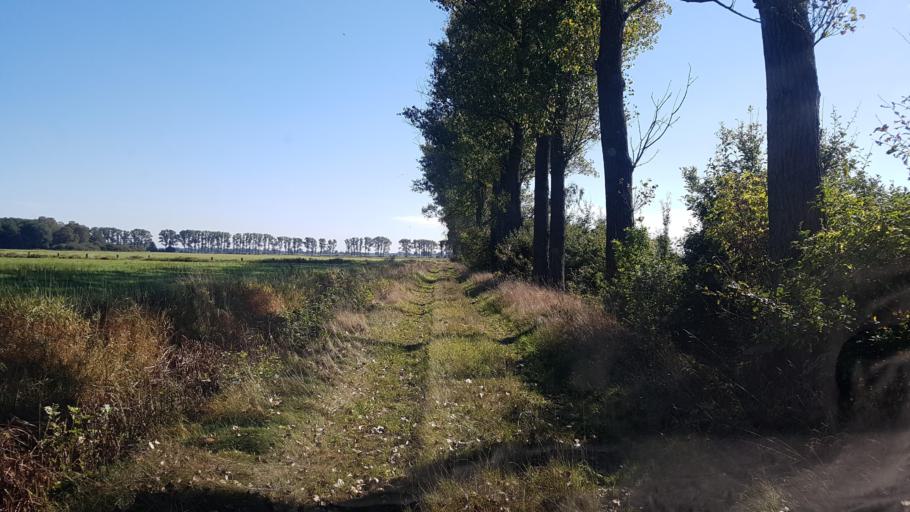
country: DE
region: Brandenburg
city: Hohenleipisch
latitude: 51.4642
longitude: 13.5722
